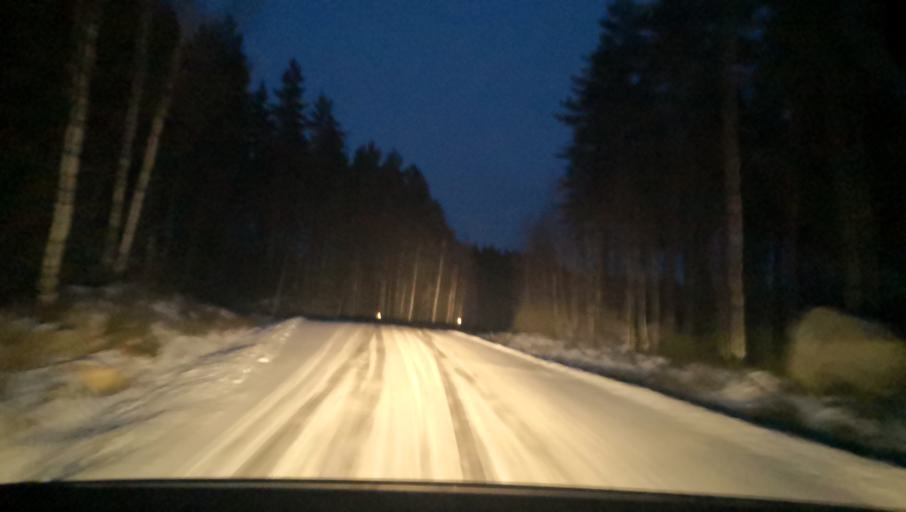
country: SE
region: Uppsala
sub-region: Heby Kommun
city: Tarnsjo
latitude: 60.2524
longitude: 16.7608
